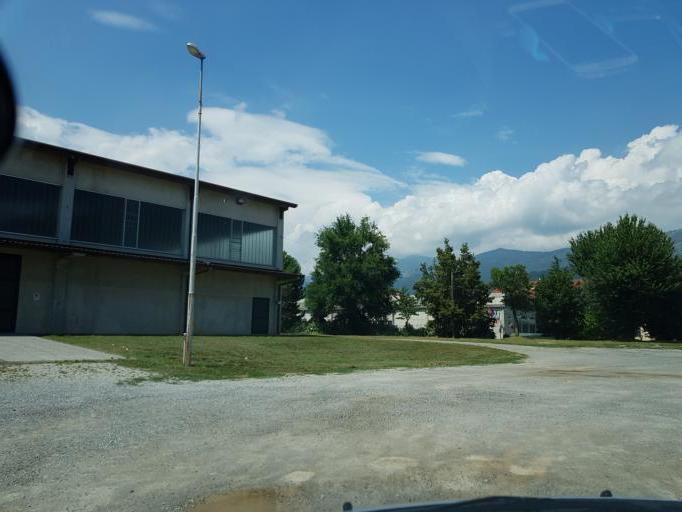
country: IT
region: Piedmont
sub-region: Provincia di Cuneo
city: Dronero
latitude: 44.4590
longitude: 7.3713
